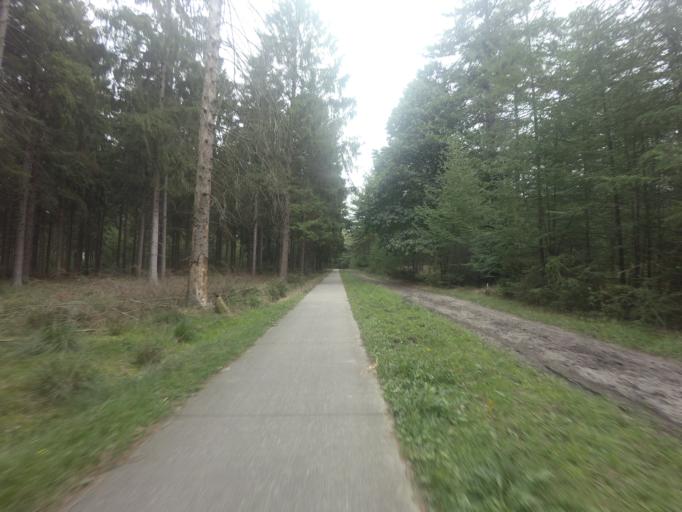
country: NL
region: Drenthe
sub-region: Gemeente Westerveld
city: Dwingeloo
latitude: 52.8939
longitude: 6.2942
